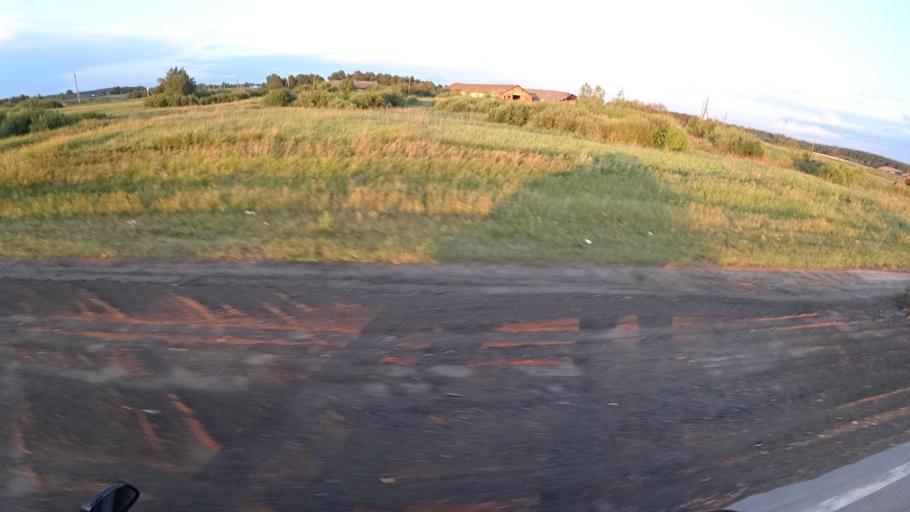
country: RU
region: Sverdlovsk
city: Kamyshlov
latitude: 56.8755
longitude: 62.7120
